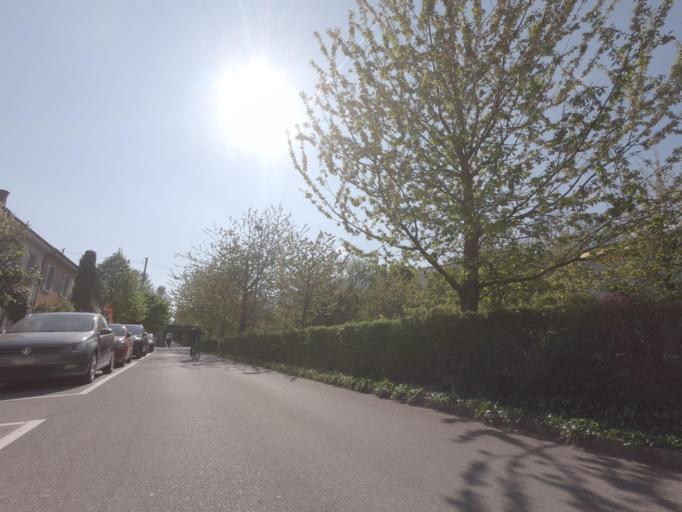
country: CH
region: Bern
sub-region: Biel/Bienne District
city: Biel/Bienne
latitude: 47.1342
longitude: 7.2401
